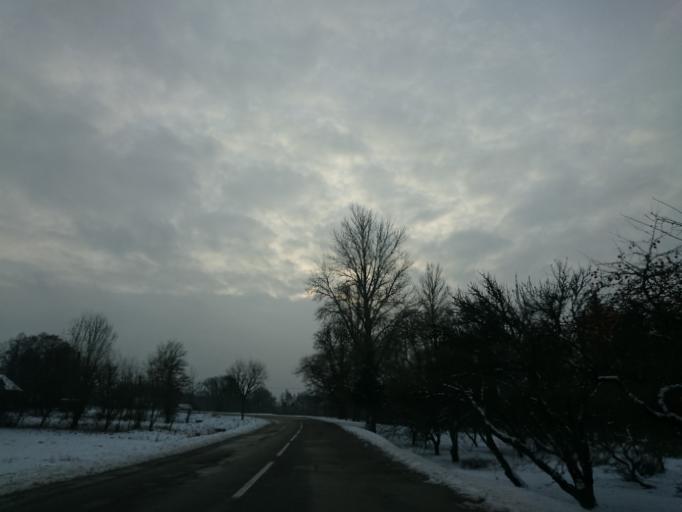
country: LV
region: Seja
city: Loja
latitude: 57.2008
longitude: 24.5931
